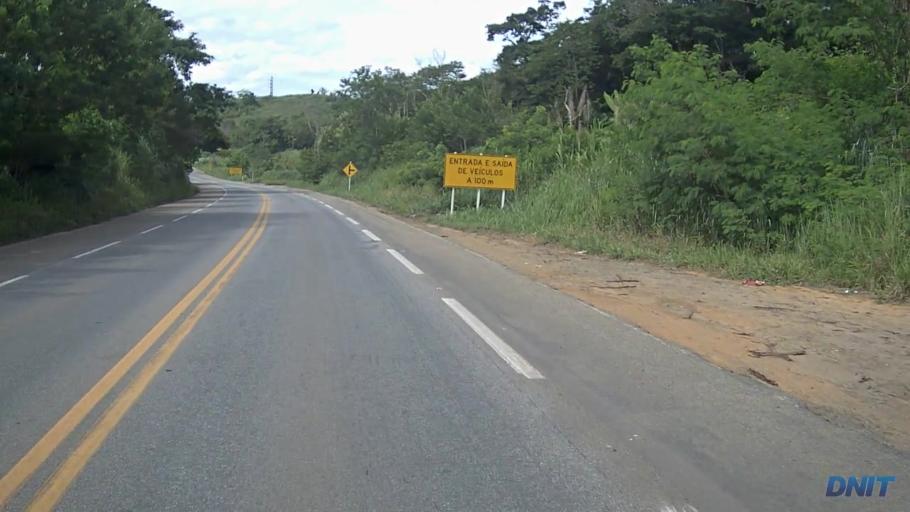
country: BR
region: Minas Gerais
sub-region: Ipaba
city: Ipaba
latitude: -19.3382
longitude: -42.4267
